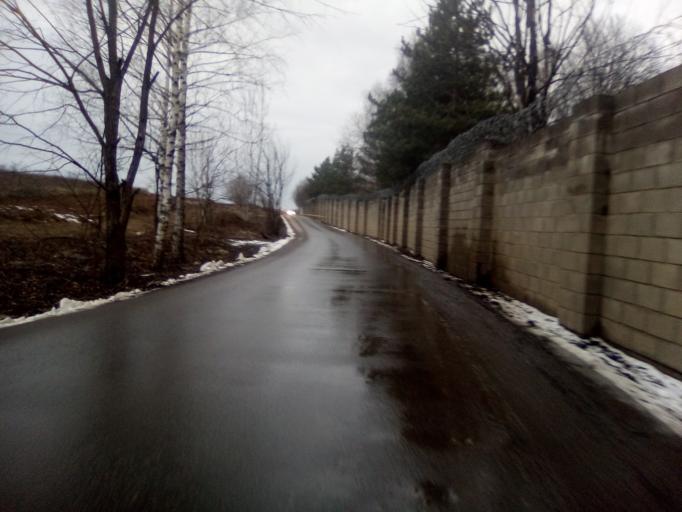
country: RU
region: Moskovskaya
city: Kommunarka
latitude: 55.5062
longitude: 37.4316
